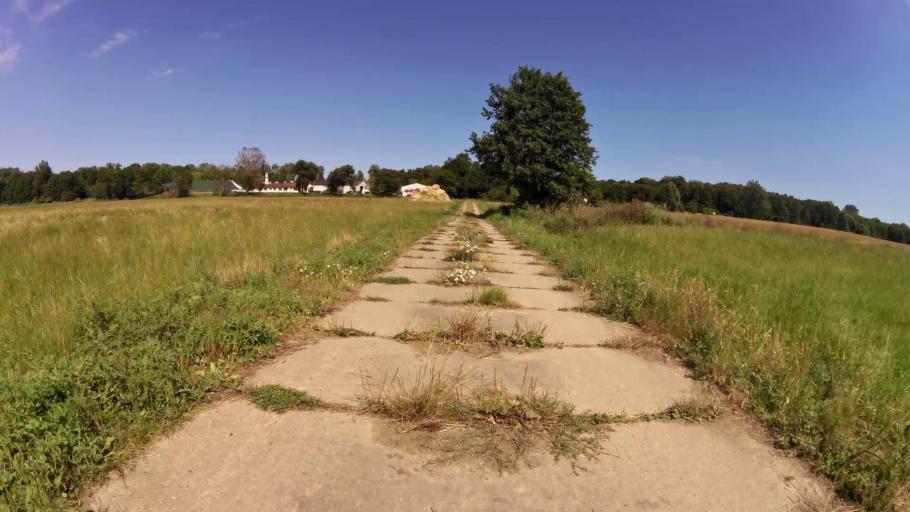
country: PL
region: West Pomeranian Voivodeship
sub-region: Powiat choszczenski
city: Choszczno
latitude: 53.2497
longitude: 15.4193
